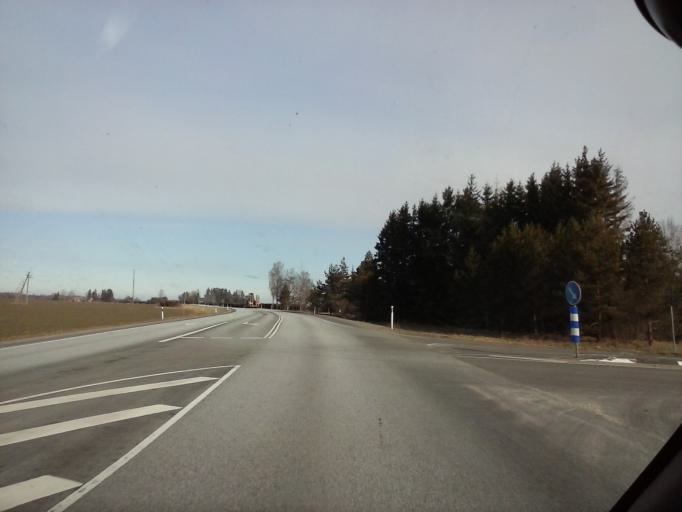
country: EE
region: Jaervamaa
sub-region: Paide linn
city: Paide
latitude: 58.8415
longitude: 25.7405
